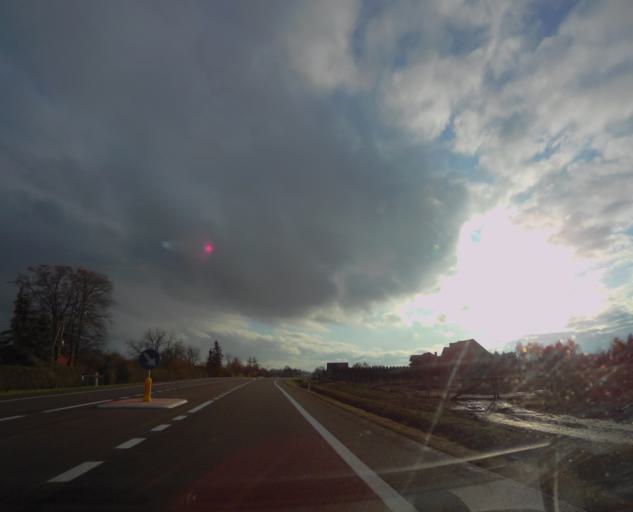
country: PL
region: Subcarpathian Voivodeship
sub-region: Powiat przemyski
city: Orly
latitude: 49.8879
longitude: 22.8162
